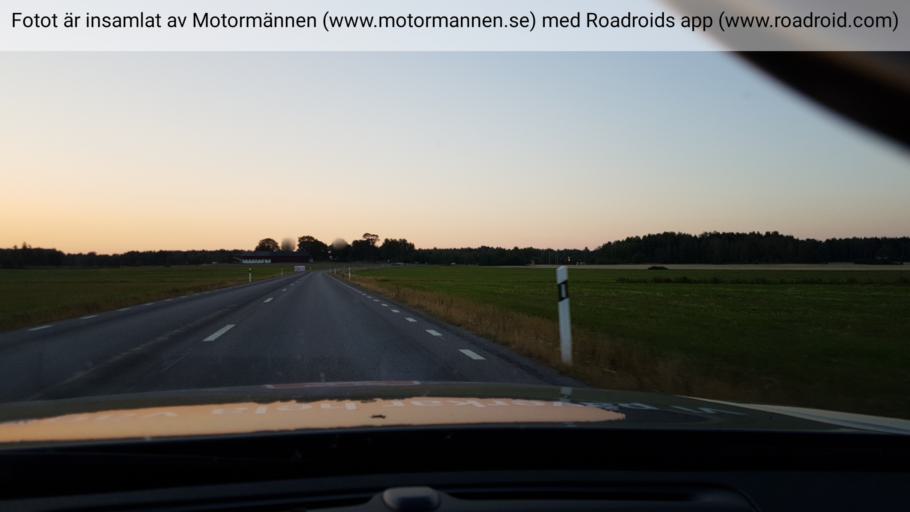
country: SE
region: Uppsala
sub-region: Heby Kommun
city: OEstervala
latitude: 60.0933
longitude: 17.1882
